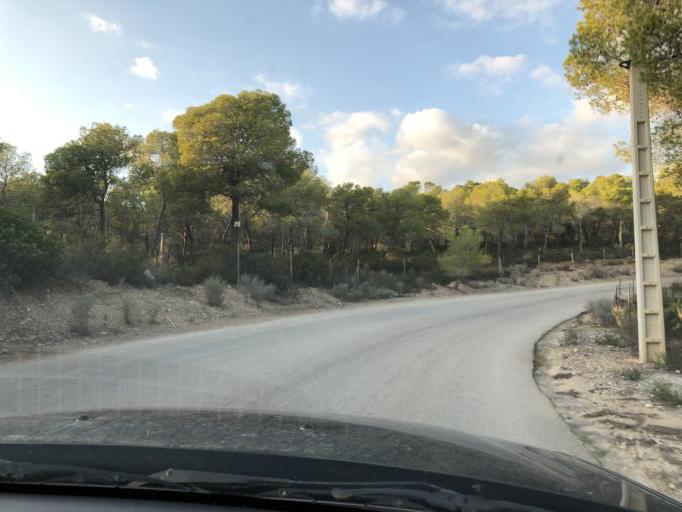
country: ES
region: Balearic Islands
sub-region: Illes Balears
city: Santa Ponsa
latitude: 39.5333
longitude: 2.4799
